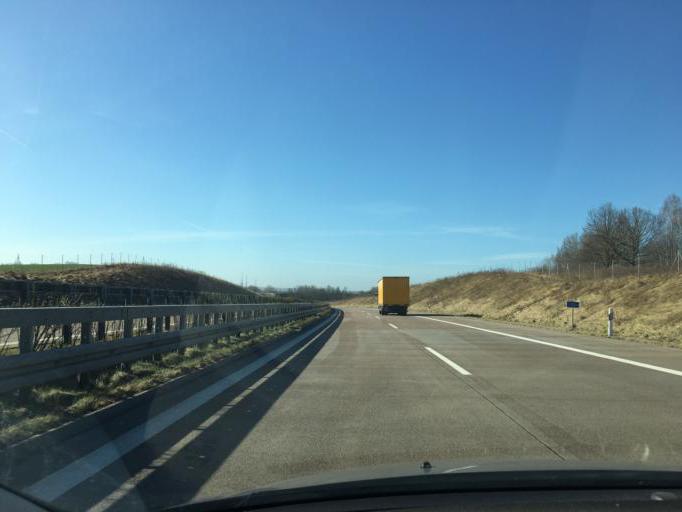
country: DE
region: Saxony
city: Penig
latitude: 50.9657
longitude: 12.6902
